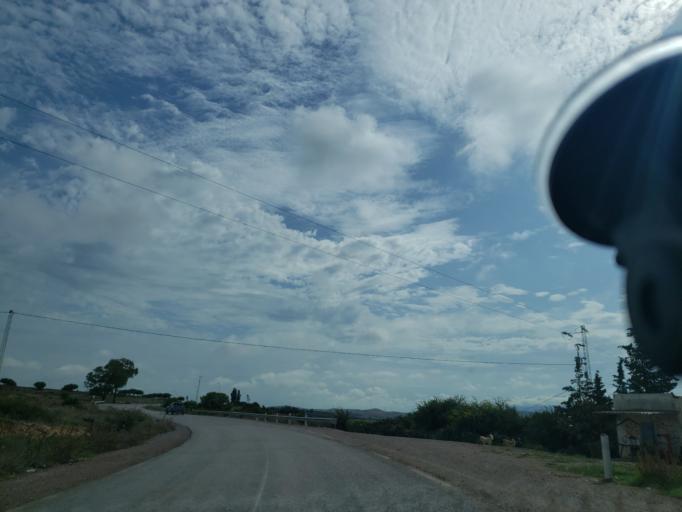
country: TN
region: Zaghwan
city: El Fahs
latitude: 36.3939
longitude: 9.9068
